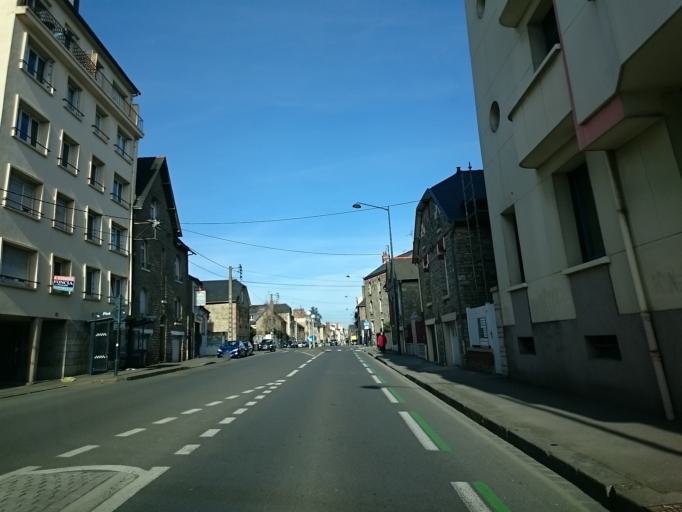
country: FR
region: Brittany
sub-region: Departement d'Ille-et-Vilaine
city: Rennes
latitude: 48.0993
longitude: -1.6572
